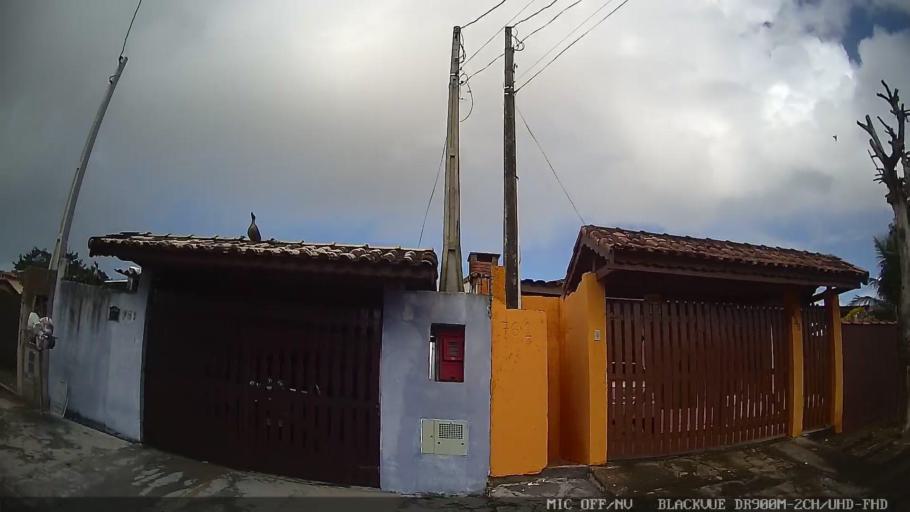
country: BR
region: Sao Paulo
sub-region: Itanhaem
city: Itanhaem
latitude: -24.2246
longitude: -46.8696
